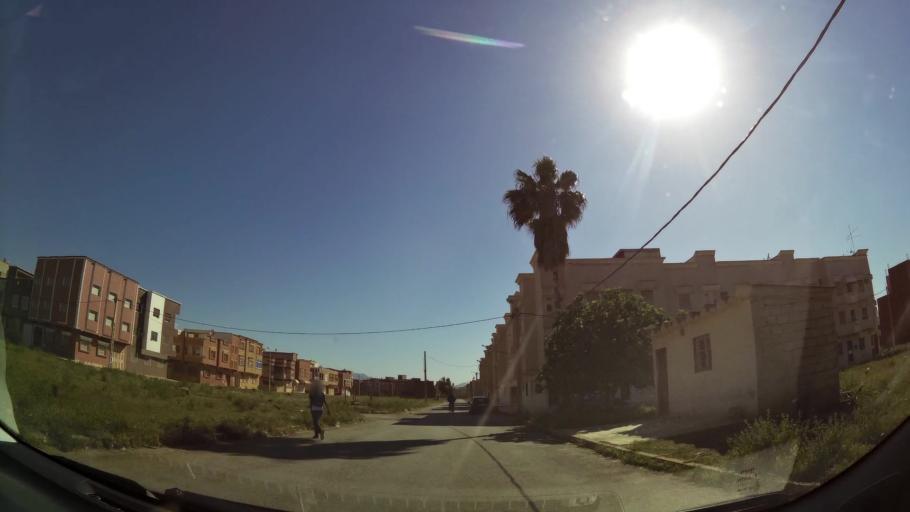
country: MA
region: Oriental
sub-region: Berkane-Taourirt
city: Berkane
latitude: 34.9415
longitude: -2.3360
